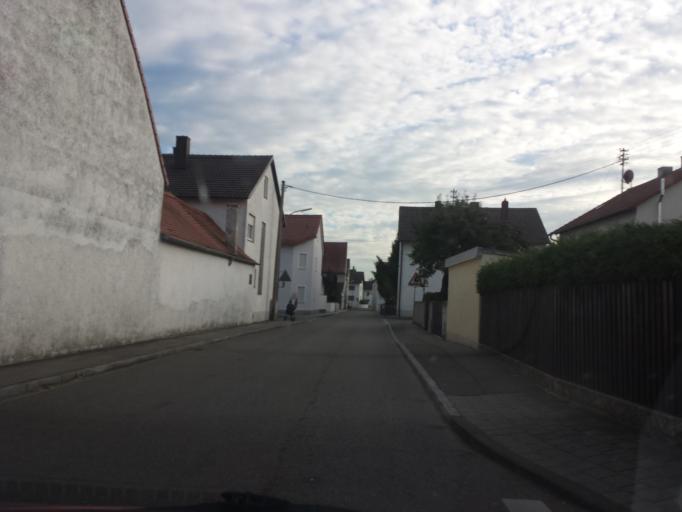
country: DE
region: Bavaria
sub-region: Upper Bavaria
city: Weichering
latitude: 48.7555
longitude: 11.3445
